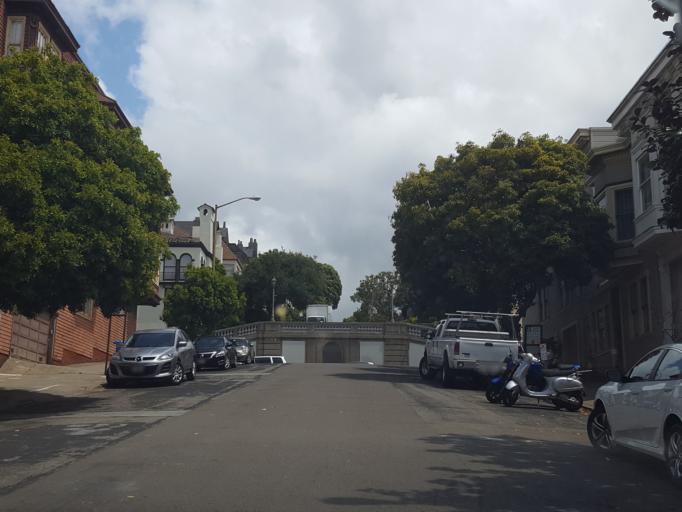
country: US
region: California
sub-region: San Francisco County
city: San Francisco
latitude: 37.7977
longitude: -122.4161
